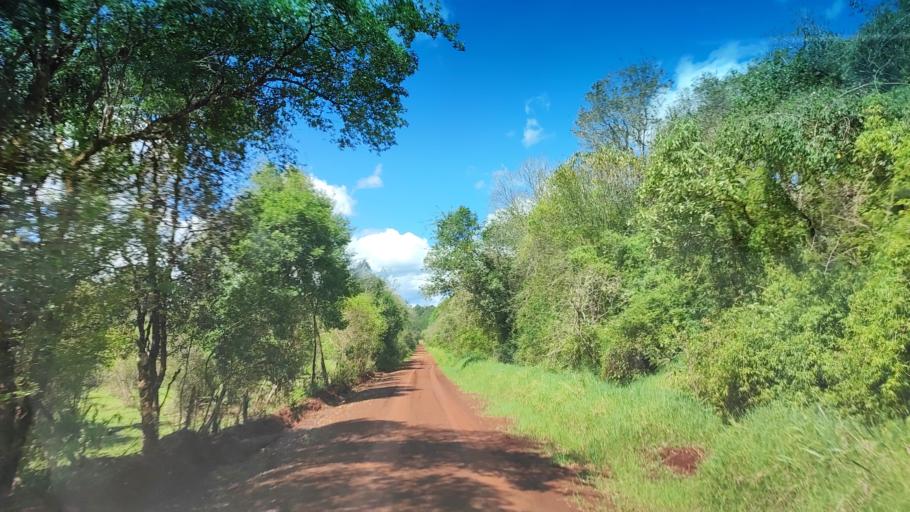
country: AR
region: Misiones
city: Capiovi
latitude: -26.9529
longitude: -55.0394
